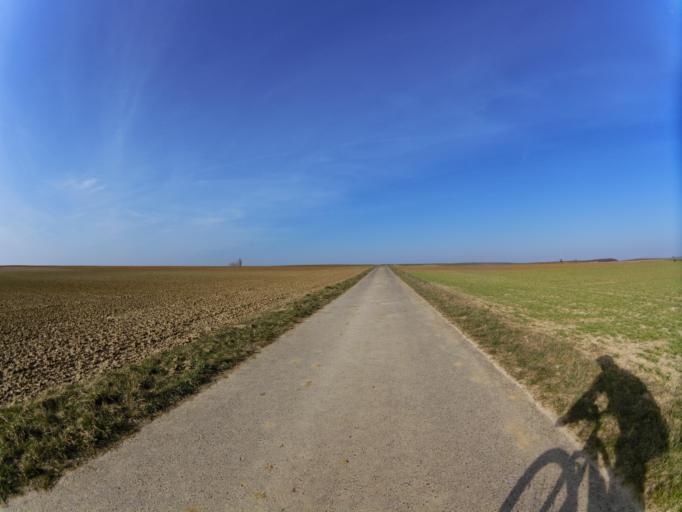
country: DE
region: Bavaria
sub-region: Regierungsbezirk Unterfranken
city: Prosselsheim
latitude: 49.8280
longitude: 10.1322
